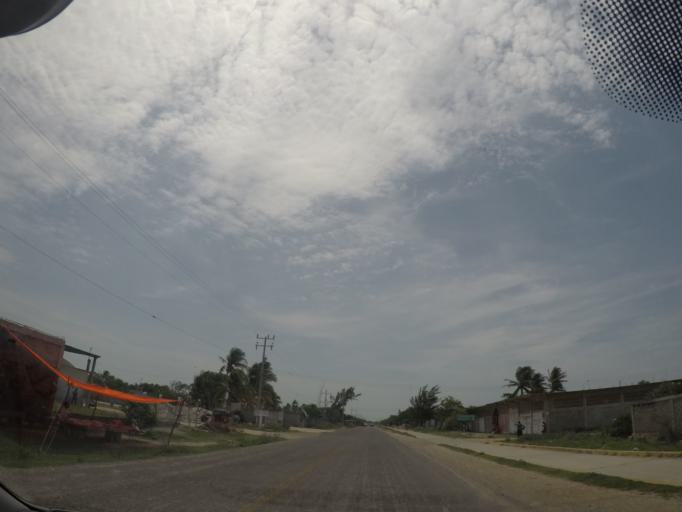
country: MX
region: Oaxaca
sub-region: San Mateo del Mar
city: Colonia Juarez
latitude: 16.2091
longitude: -95.0280
